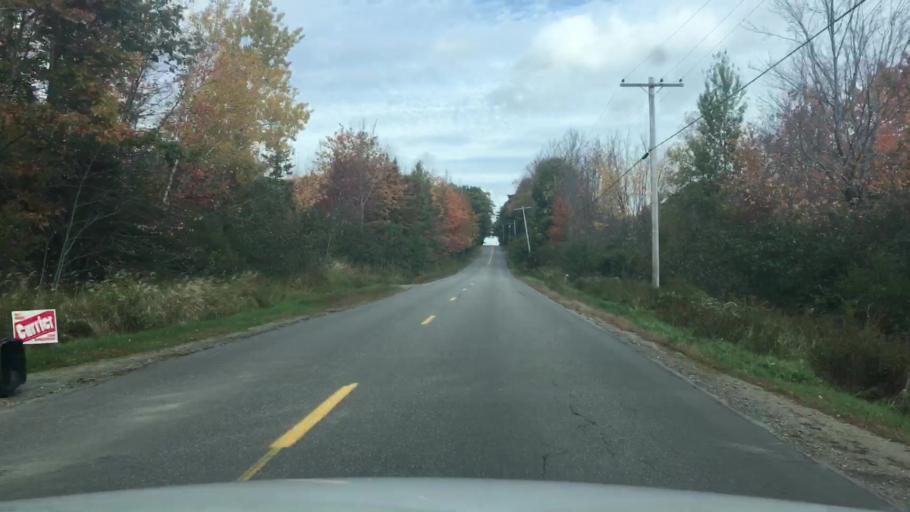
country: US
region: Maine
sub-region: Waldo County
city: Searsmont
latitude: 44.3879
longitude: -69.1332
